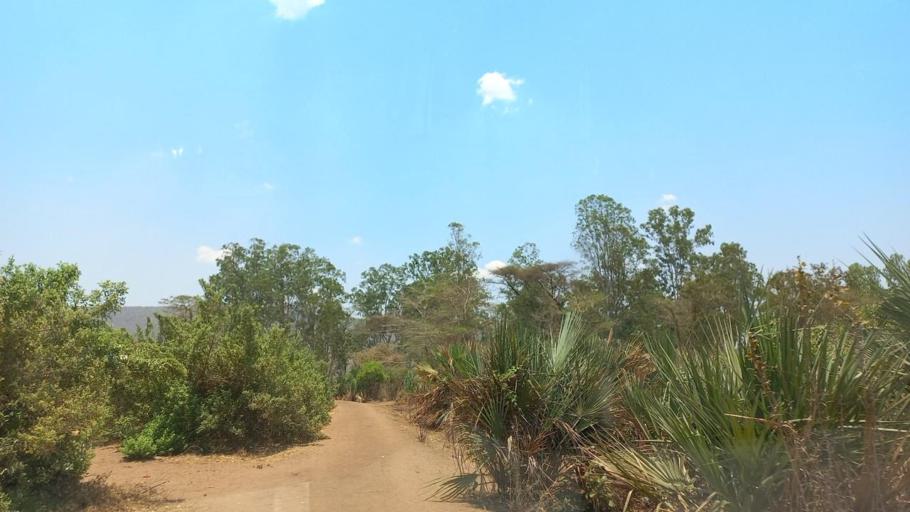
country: ZM
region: Lusaka
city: Luangwa
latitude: -15.1975
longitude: 30.1731
